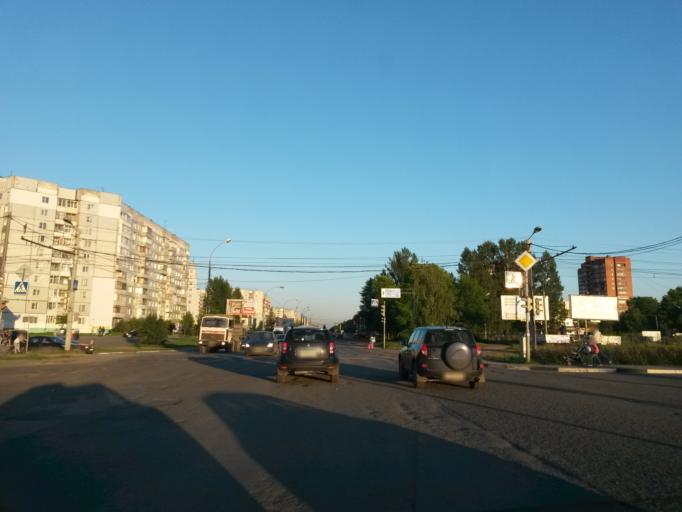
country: RU
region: Jaroslavl
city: Yaroslavl
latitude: 57.6979
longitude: 39.7640
